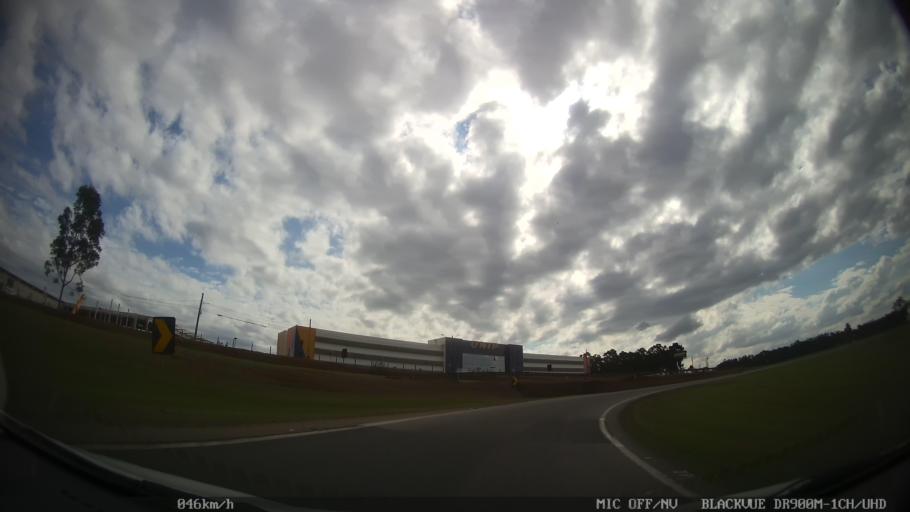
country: BR
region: Sao Paulo
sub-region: Limeira
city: Limeira
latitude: -22.5455
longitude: -47.3773
